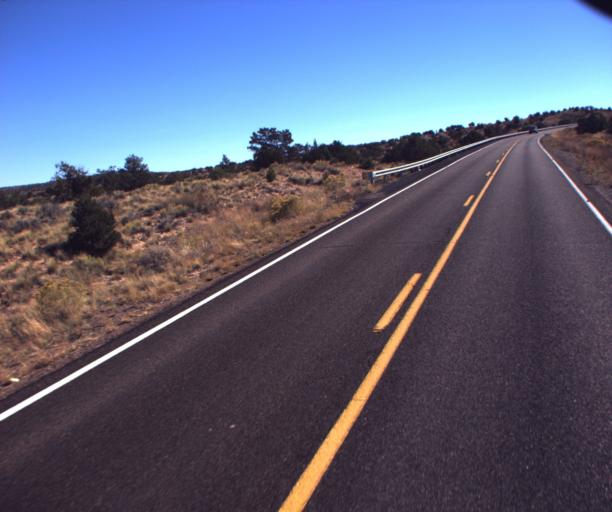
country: US
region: Arizona
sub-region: Navajo County
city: First Mesa
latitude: 35.7455
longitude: -110.1221
